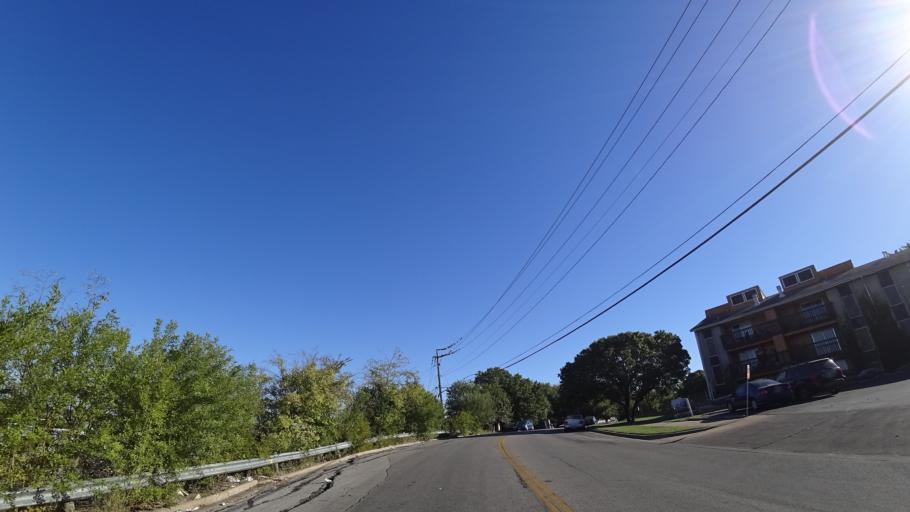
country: US
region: Texas
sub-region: Travis County
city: Austin
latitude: 30.2381
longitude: -97.7277
